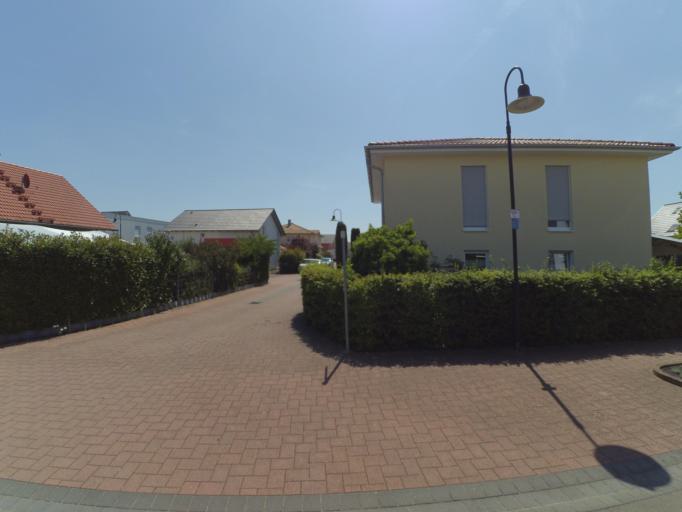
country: DE
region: Rheinland-Pfalz
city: Bornheim
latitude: 49.2191
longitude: 8.1676
